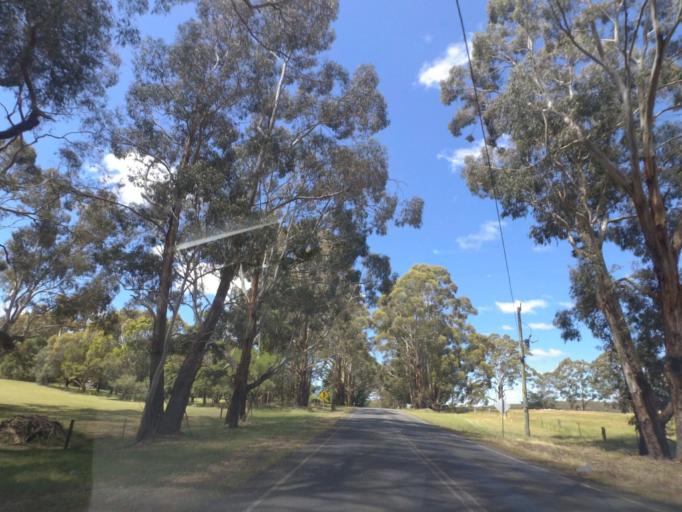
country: AU
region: Victoria
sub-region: Mount Alexander
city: Castlemaine
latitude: -37.3162
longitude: 144.2195
